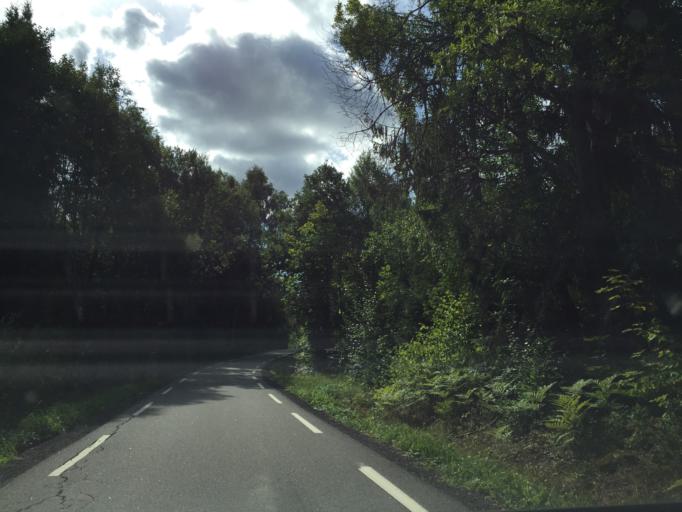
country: NO
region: Vestfold
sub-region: Holmestrand
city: Gullhaug
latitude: 59.4375
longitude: 10.1615
